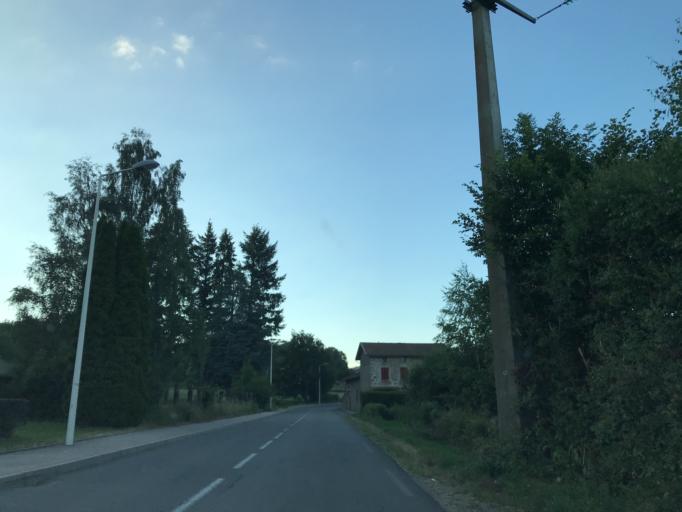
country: FR
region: Rhone-Alpes
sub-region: Departement de la Loire
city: Noiretable
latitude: 45.8081
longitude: 3.7693
